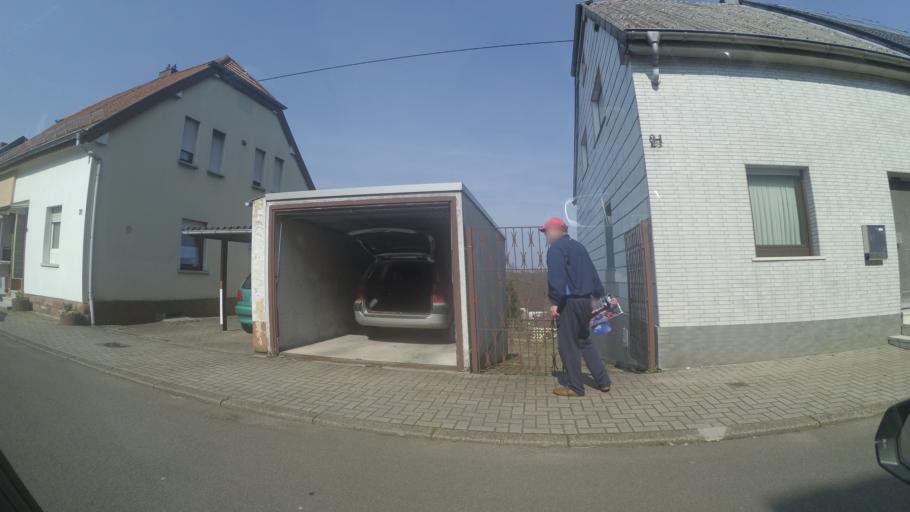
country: DE
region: Saarland
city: Quierschied
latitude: 49.3114
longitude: 7.0588
